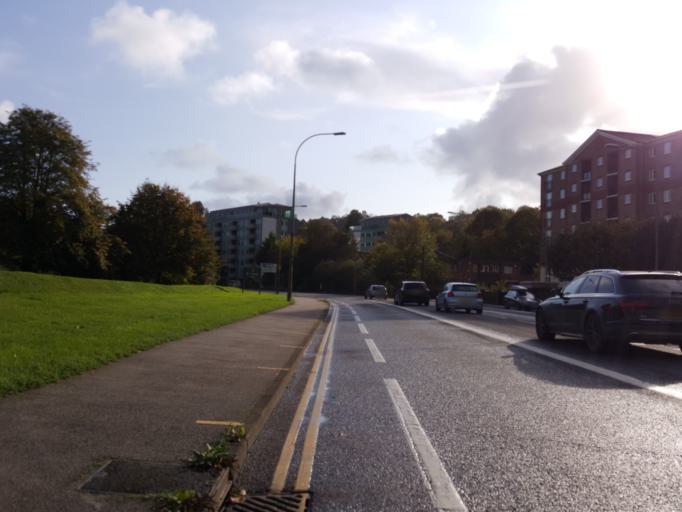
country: GB
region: England
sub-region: Brighton and Hove
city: Hove
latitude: 50.8548
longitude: -0.1547
